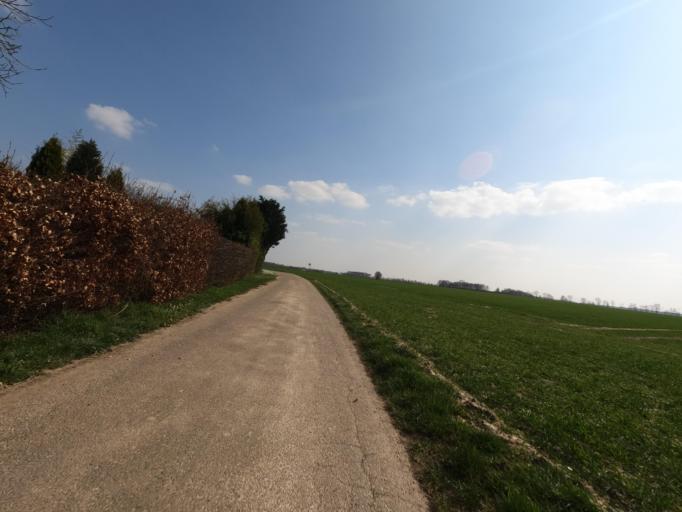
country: DE
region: North Rhine-Westphalia
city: Erkelenz
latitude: 51.0765
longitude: 6.2858
